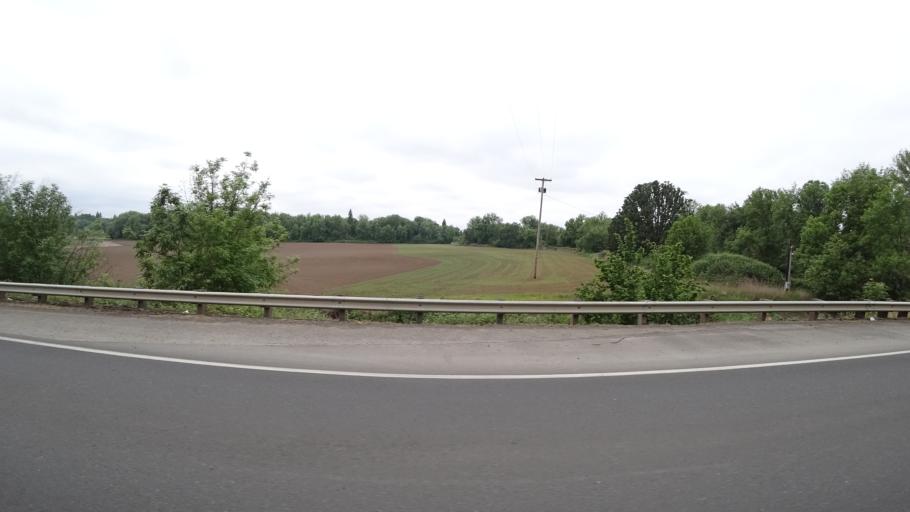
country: US
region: Oregon
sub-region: Washington County
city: Hillsboro
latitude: 45.4998
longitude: -122.9915
